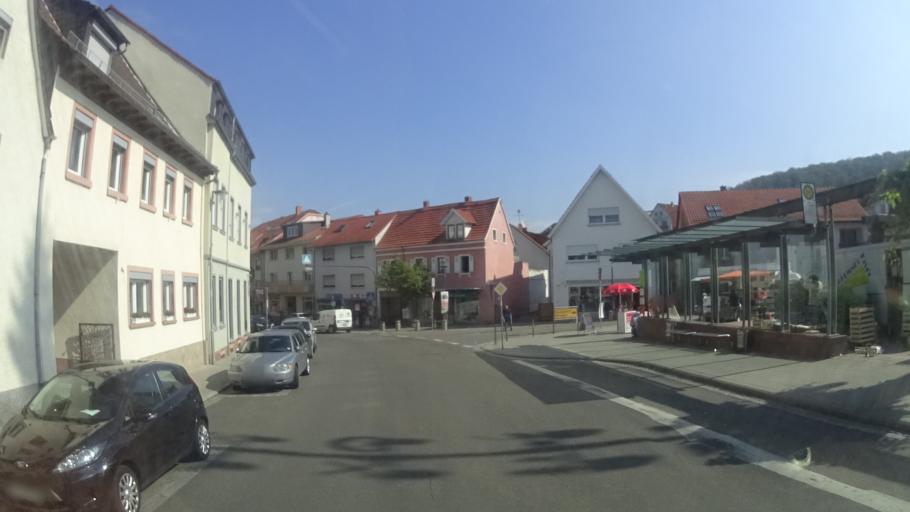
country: DE
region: Baden-Wuerttemberg
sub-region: Karlsruhe Region
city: Nussloch
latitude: 49.3226
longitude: 8.6958
